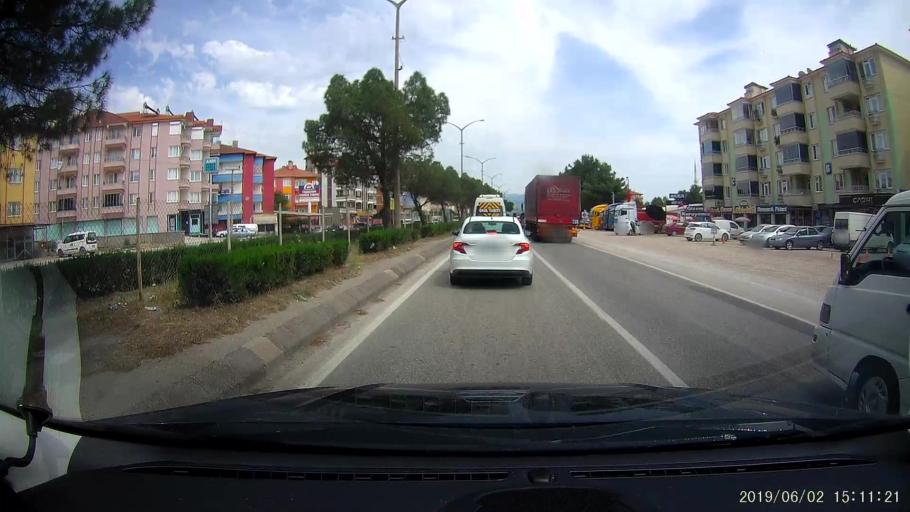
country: TR
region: Corum
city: Osmancik
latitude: 40.9780
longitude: 34.8081
